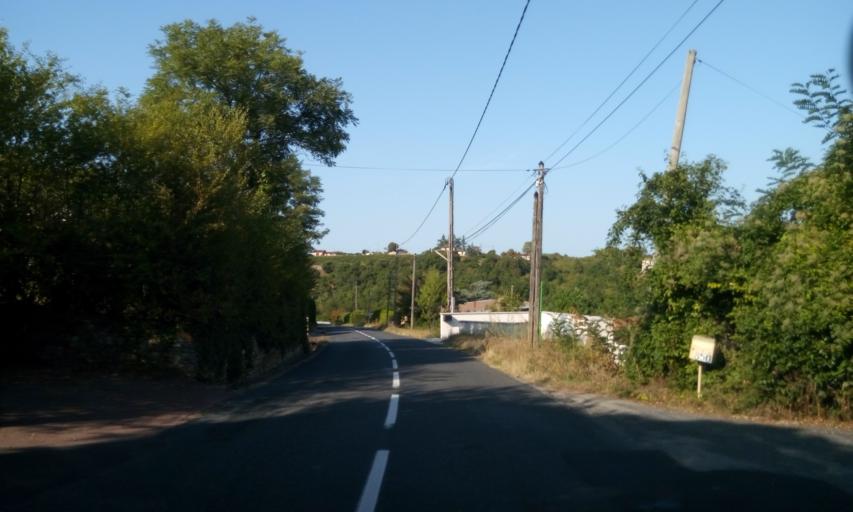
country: FR
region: Rhone-Alpes
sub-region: Departement du Rhone
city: Lucenay
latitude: 45.9301
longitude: 4.6964
